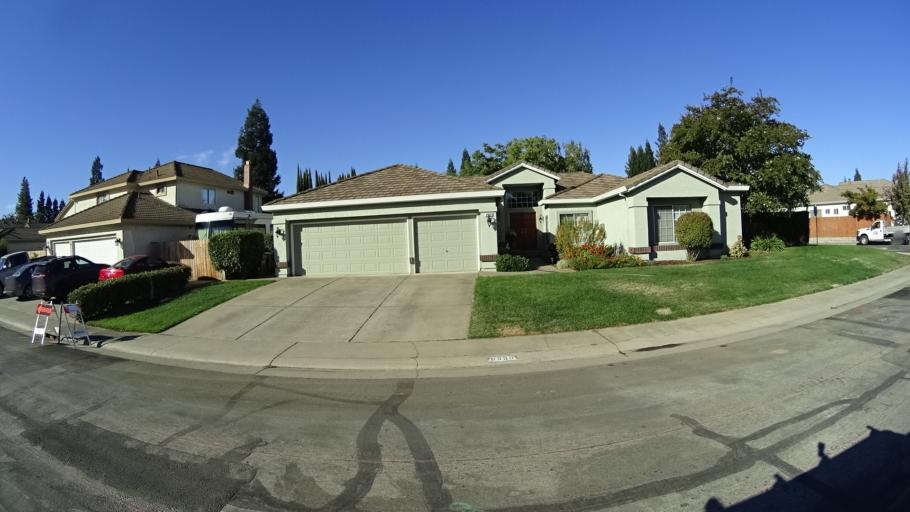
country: US
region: California
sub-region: Sacramento County
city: Elk Grove
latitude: 38.4316
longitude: -121.3748
